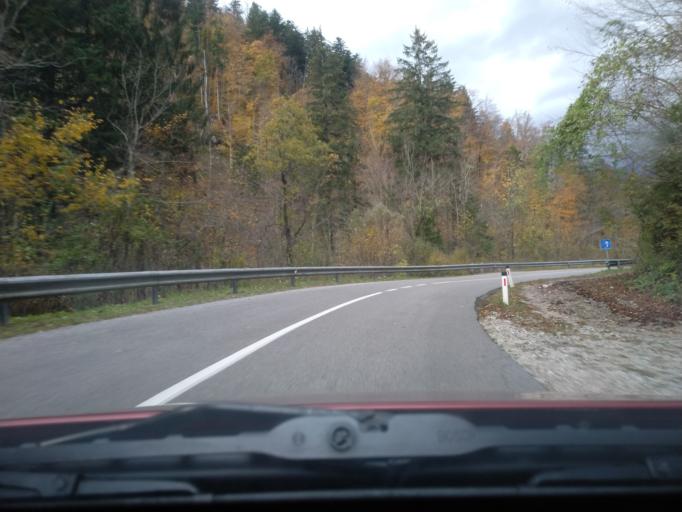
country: SI
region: Kamnik
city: Mekinje
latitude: 46.2884
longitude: 14.6160
